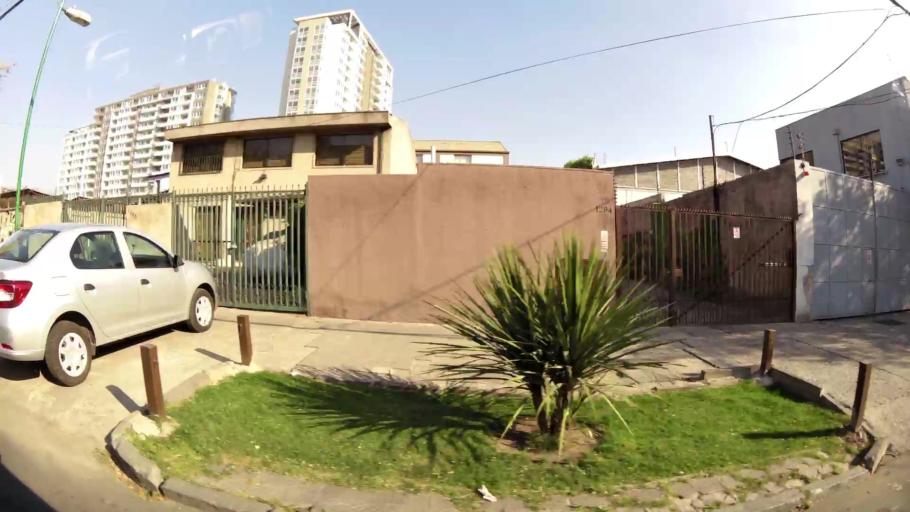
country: CL
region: Santiago Metropolitan
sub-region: Provincia de Santiago
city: Santiago
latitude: -33.4177
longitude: -70.6578
